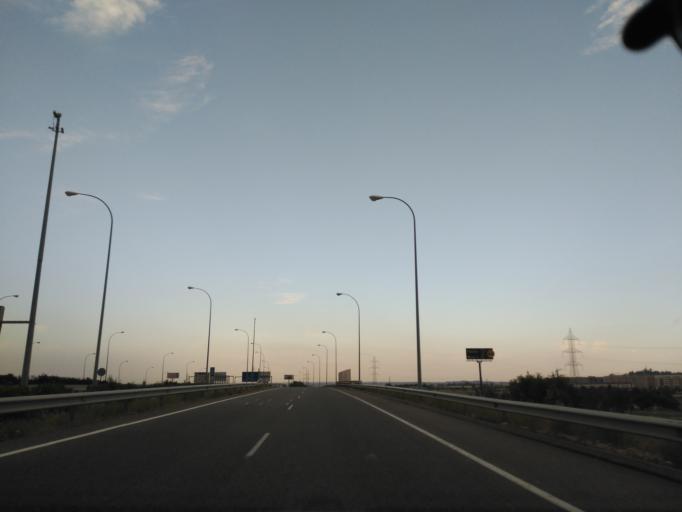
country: ES
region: Madrid
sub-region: Provincia de Madrid
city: Villaverde
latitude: 40.3257
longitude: -3.7093
